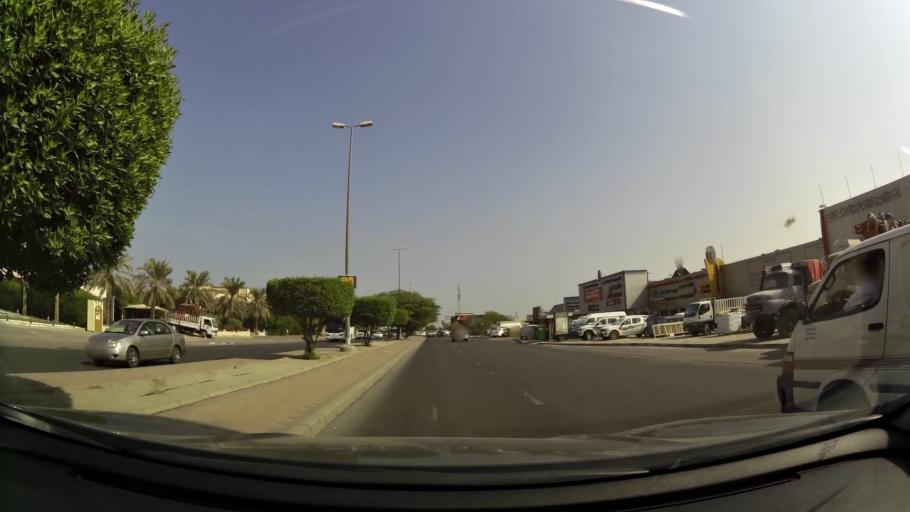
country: KW
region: Al Ahmadi
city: Al Fahahil
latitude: 29.0735
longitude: 48.1201
